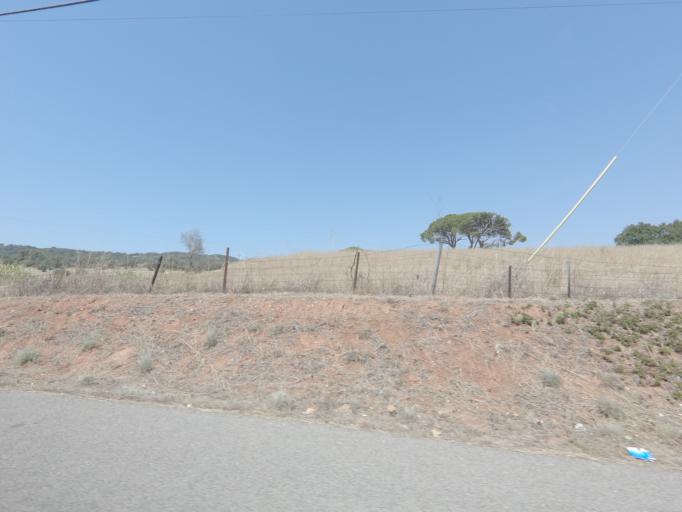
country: PT
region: Setubal
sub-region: Setubal
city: Setubal
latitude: 38.5329
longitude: -8.9061
